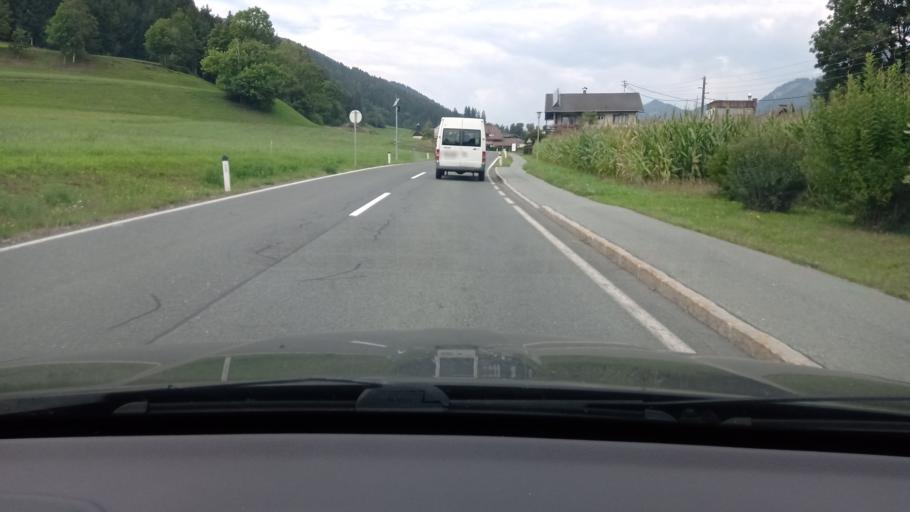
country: AT
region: Carinthia
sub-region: Politischer Bezirk Hermagor
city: Hermagor
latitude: 46.6328
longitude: 13.3542
